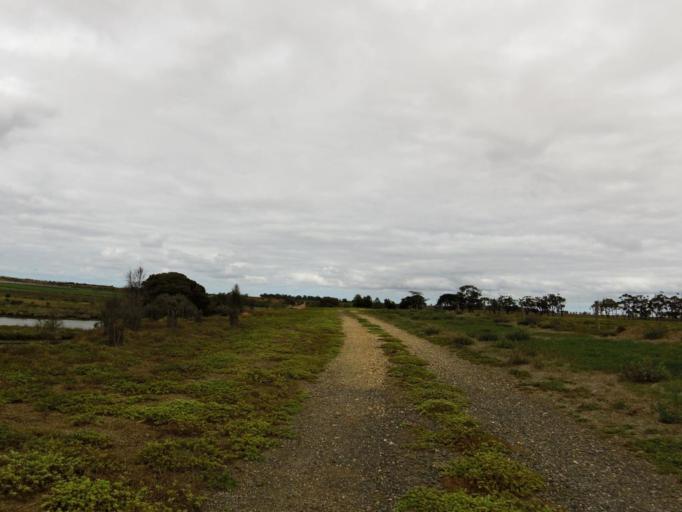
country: AU
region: Victoria
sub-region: Wyndham
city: Werribee
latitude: -37.9463
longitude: 144.6641
